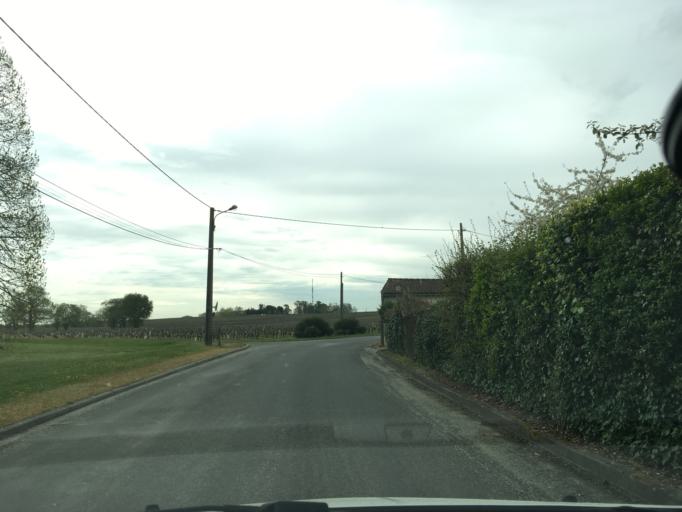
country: FR
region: Aquitaine
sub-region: Departement de la Gironde
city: Lesparre-Medoc
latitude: 45.3131
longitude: -0.8927
